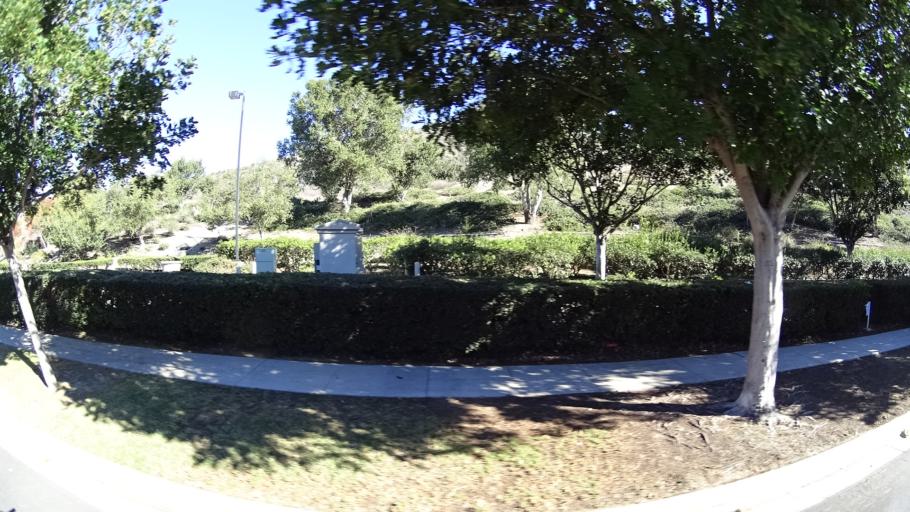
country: US
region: California
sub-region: Orange County
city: Ladera Ranch
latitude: 33.5591
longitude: -117.6280
